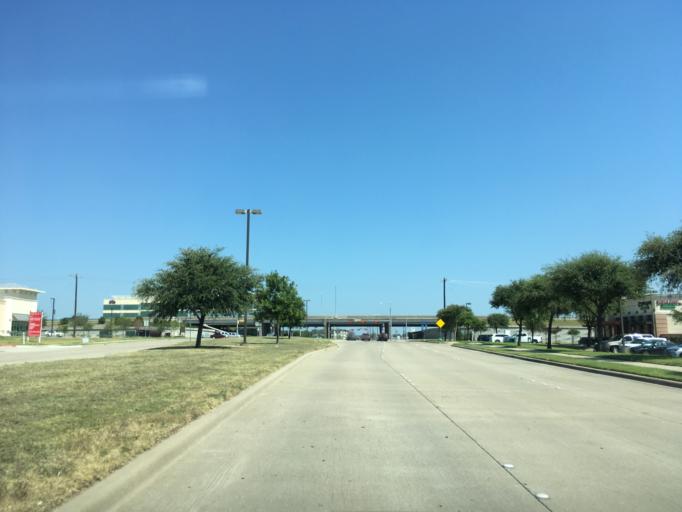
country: US
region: Texas
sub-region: Collin County
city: Allen
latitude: 33.1429
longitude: -96.6781
